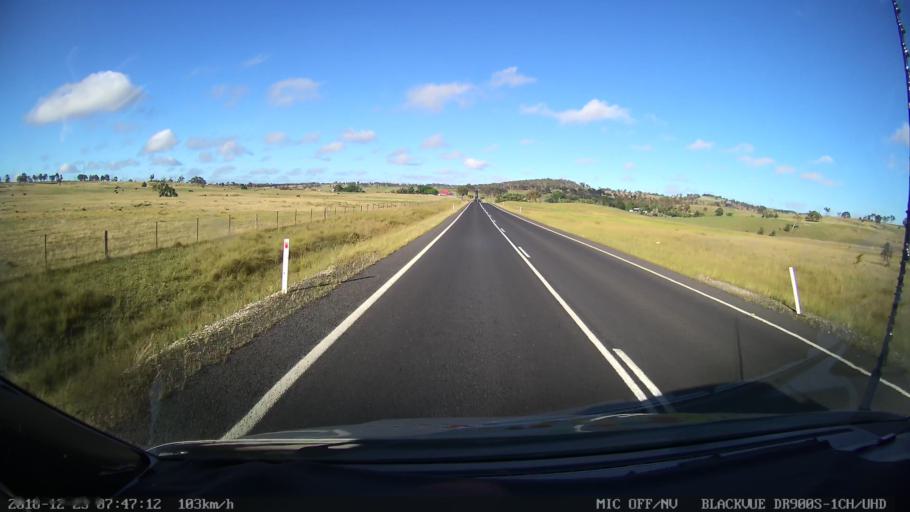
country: AU
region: New South Wales
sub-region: Armidale Dumaresq
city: Enmore
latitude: -30.5258
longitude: 151.9054
